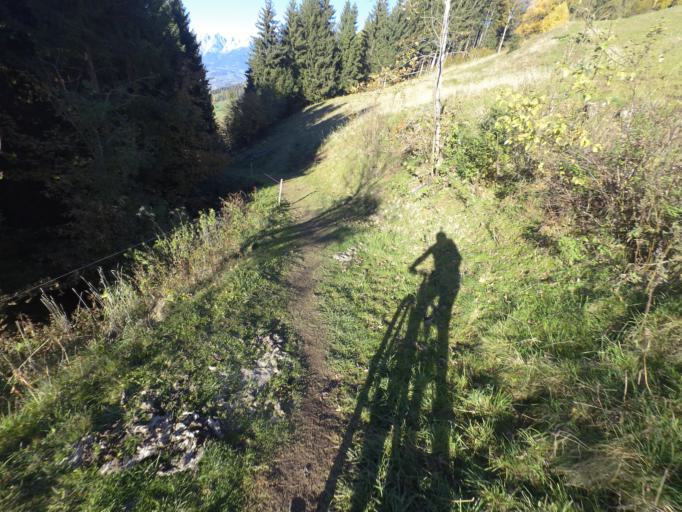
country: AT
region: Salzburg
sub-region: Politischer Bezirk Sankt Johann im Pongau
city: Sankt Johann im Pongau
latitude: 47.3410
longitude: 13.2195
